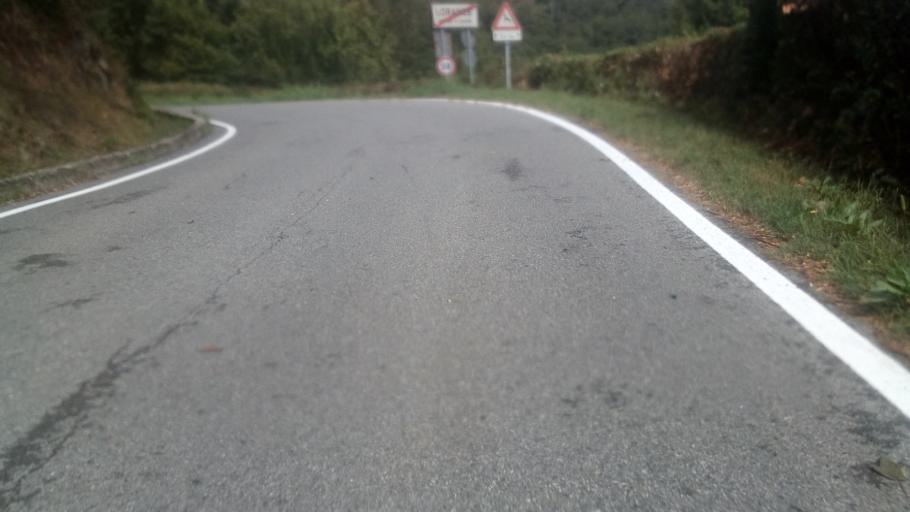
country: IT
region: Piedmont
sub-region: Provincia di Torino
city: Loranze
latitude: 45.4403
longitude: 7.8056
